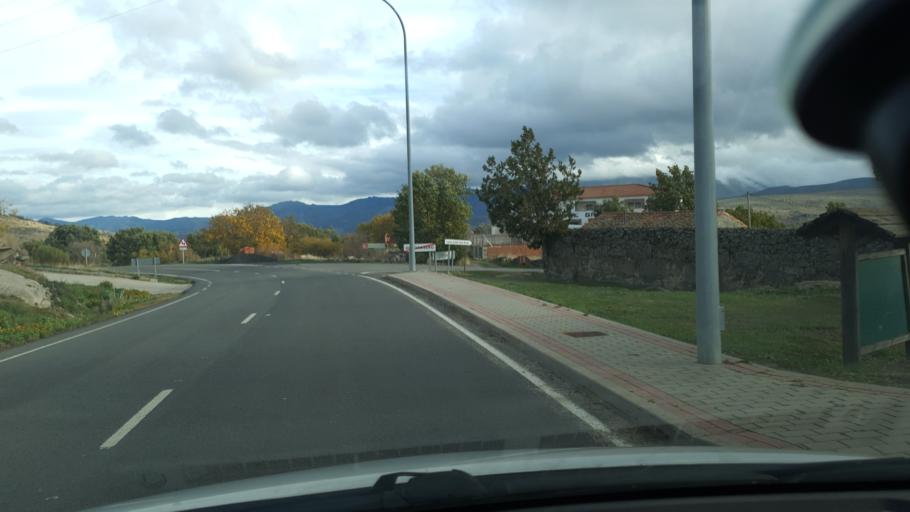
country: ES
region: Castille and Leon
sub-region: Provincia de Avila
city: Hoyocasero
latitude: 40.3973
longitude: -4.9746
